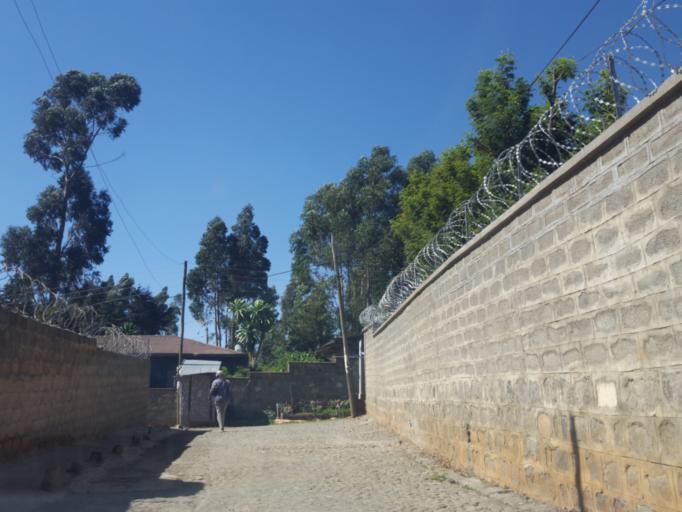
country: ET
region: Adis Abeba
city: Addis Ababa
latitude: 9.0568
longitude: 38.7453
